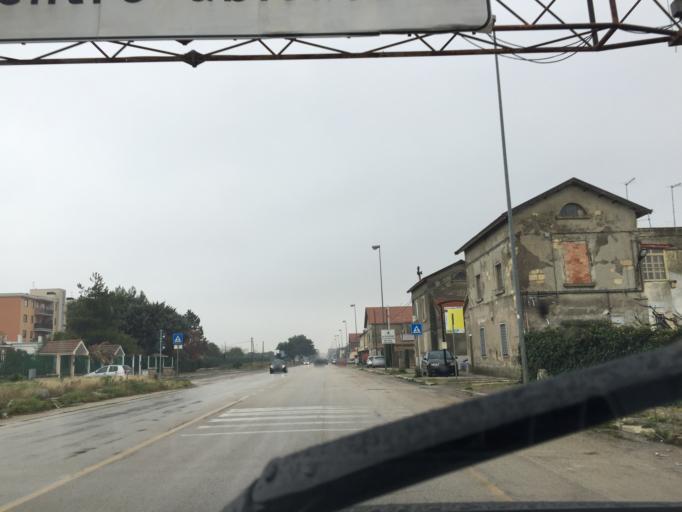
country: IT
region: Apulia
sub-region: Provincia di Foggia
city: Foggia
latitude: 41.4692
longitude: 15.5191
